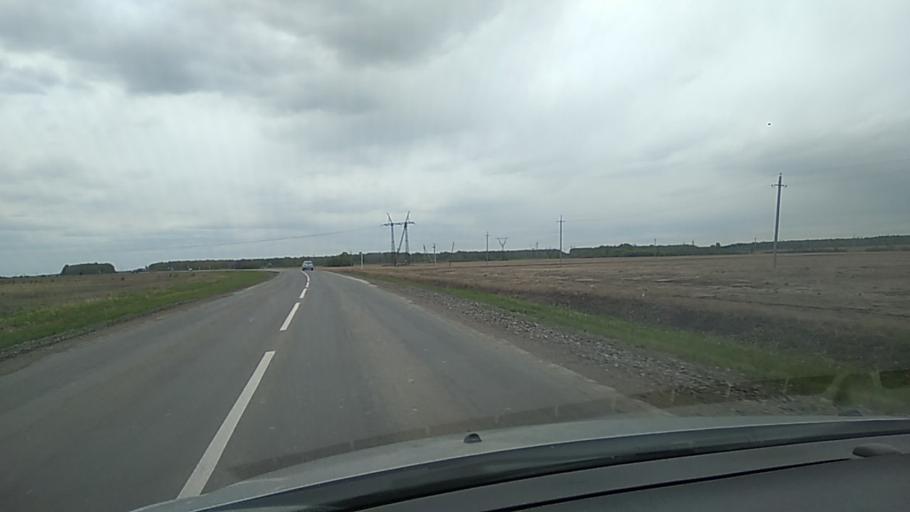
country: RU
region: Sverdlovsk
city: Martyush
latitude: 56.4108
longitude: 61.7990
